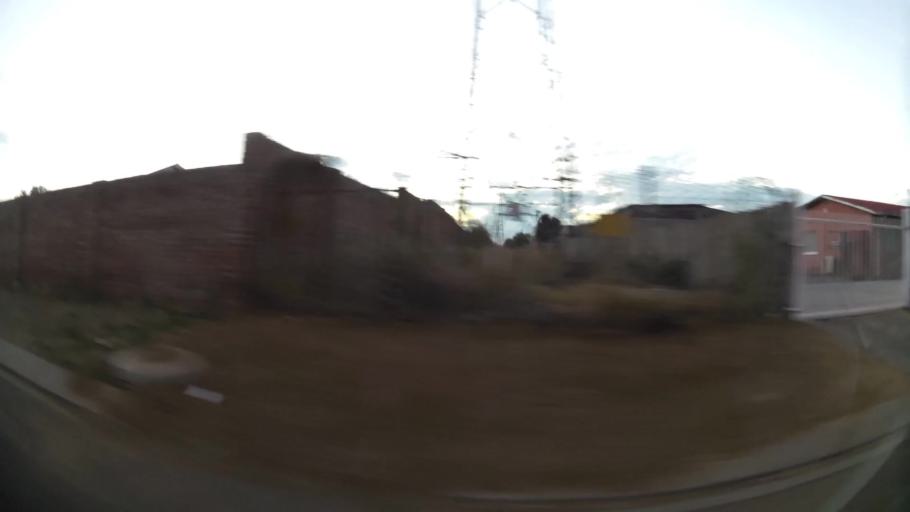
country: ZA
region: Orange Free State
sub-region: Mangaung Metropolitan Municipality
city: Bloemfontein
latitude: -29.1651
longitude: 26.2000
